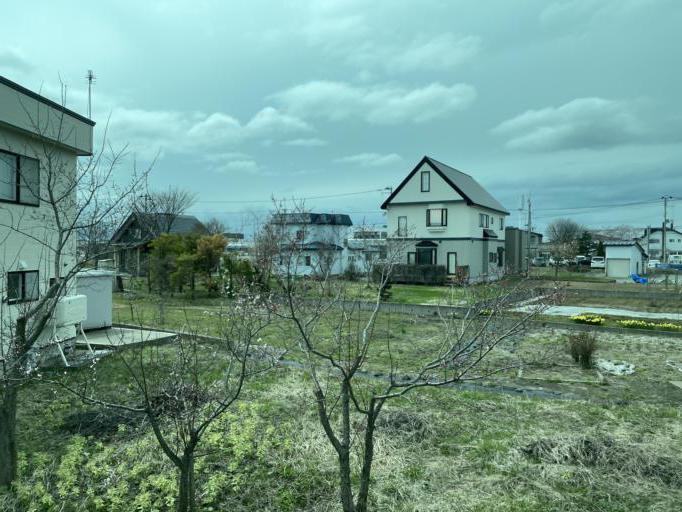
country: JP
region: Aomori
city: Goshogawara
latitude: 40.7641
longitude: 140.4352
